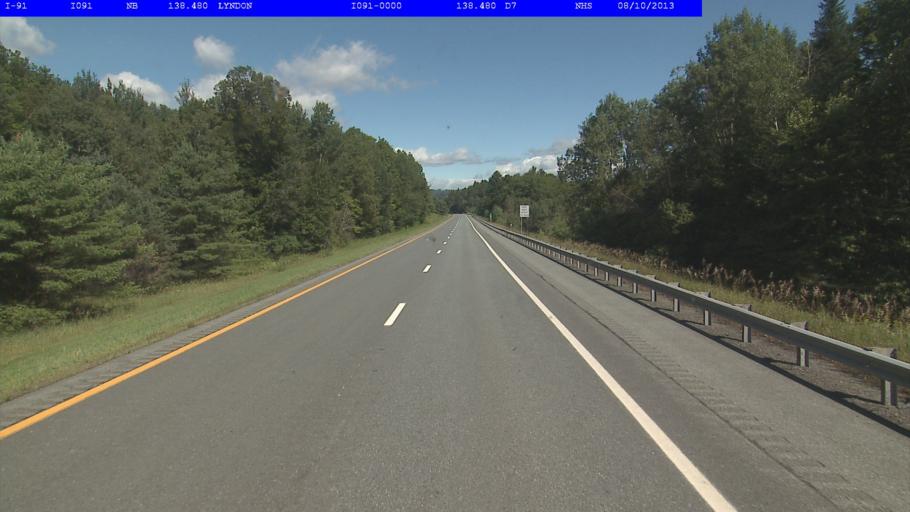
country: US
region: Vermont
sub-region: Caledonia County
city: Lyndonville
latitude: 44.5347
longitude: -72.0176
